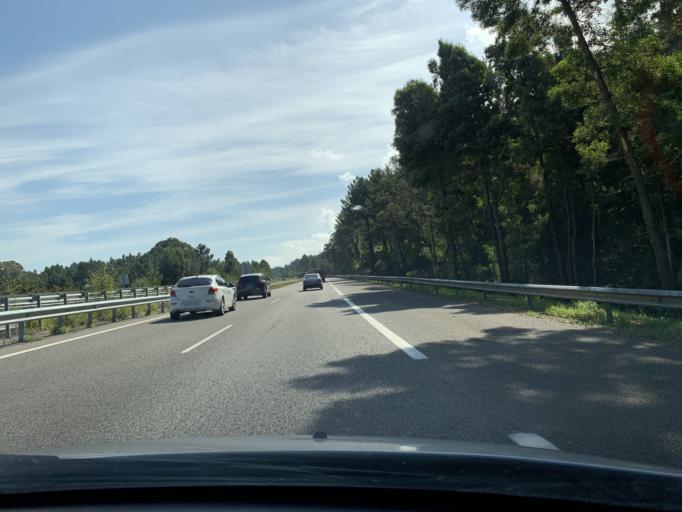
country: ES
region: Asturias
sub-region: Province of Asturias
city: Salas
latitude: 43.5411
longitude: -6.3786
